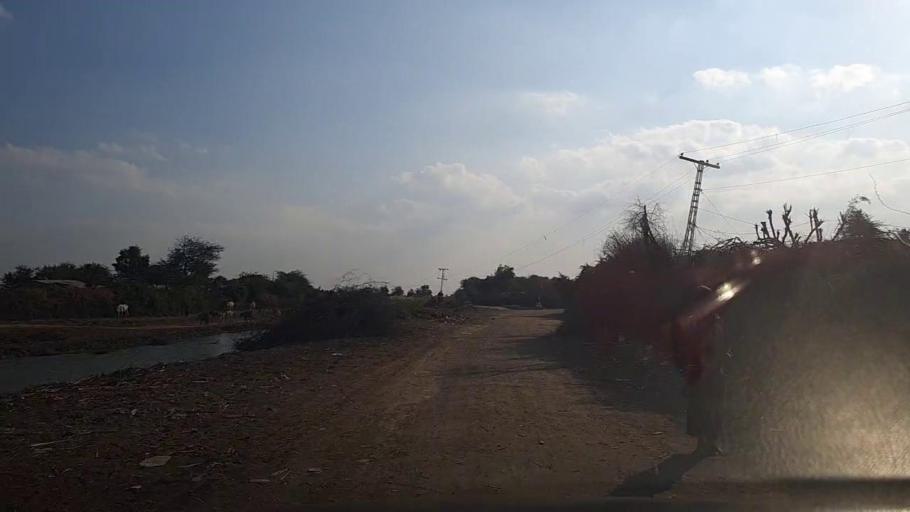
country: PK
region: Sindh
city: Jhol
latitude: 25.8373
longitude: 69.0530
